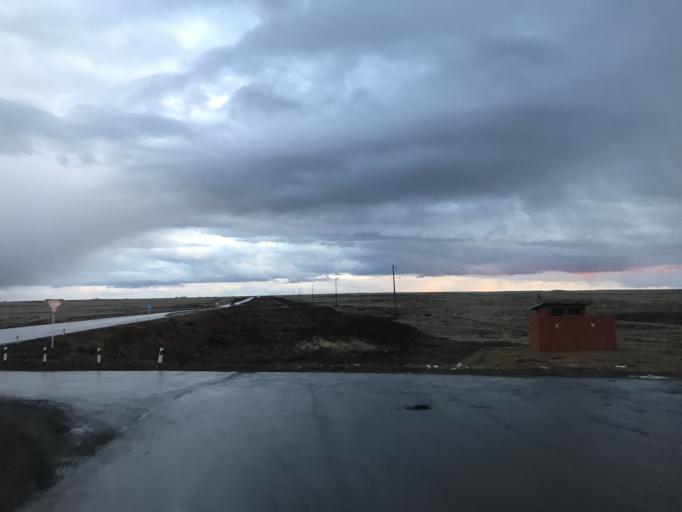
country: KZ
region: Qostanay
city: Ordzhonikidze
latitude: 52.4474
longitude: 61.7722
